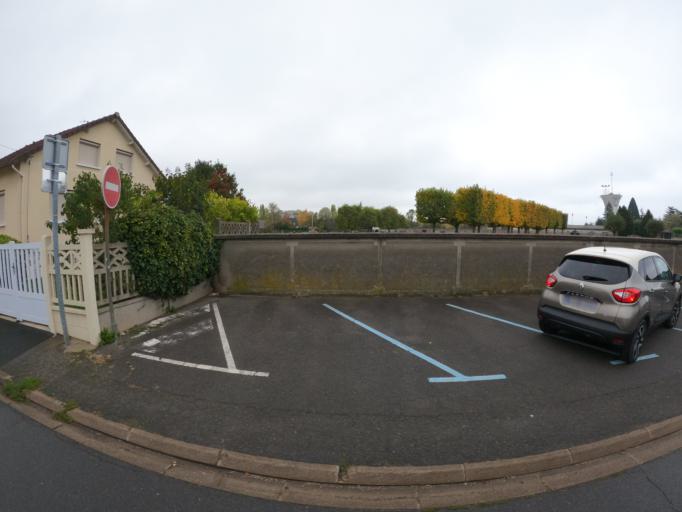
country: FR
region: Ile-de-France
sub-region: Departement du Val-de-Marne
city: Ormesson-sur-Marne
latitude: 48.7899
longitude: 2.5426
